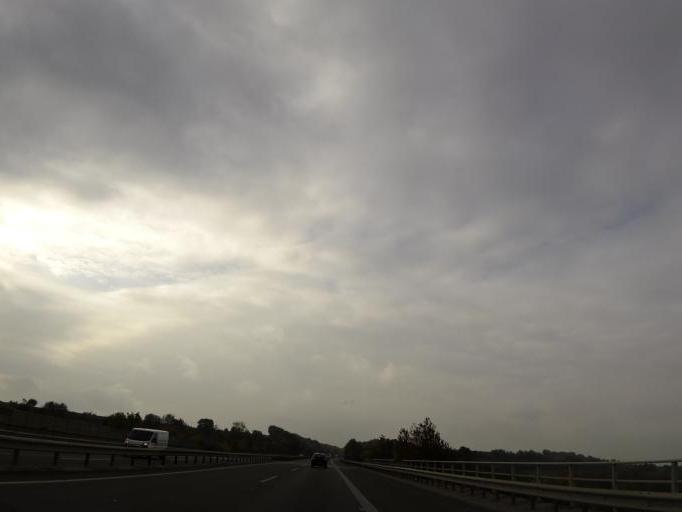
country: DE
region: Rheinland-Pfalz
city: Freimersheim
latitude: 49.7305
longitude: 8.0816
